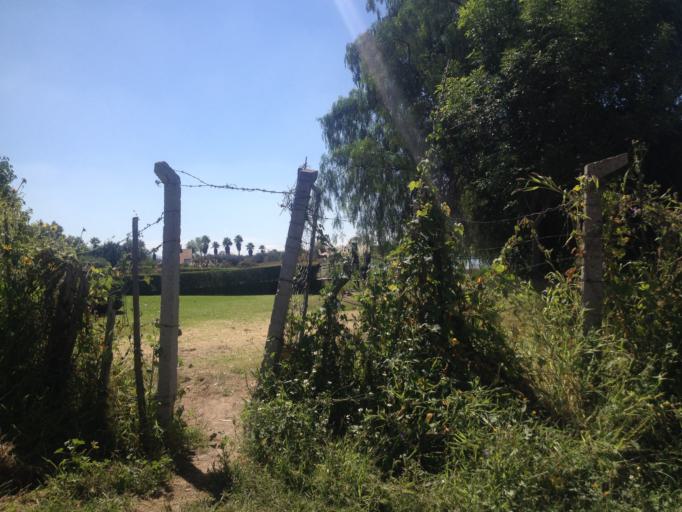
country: MX
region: Aguascalientes
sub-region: Aguascalientes
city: San Sebastian [Fraccionamiento]
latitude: 21.7879
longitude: -102.2627
